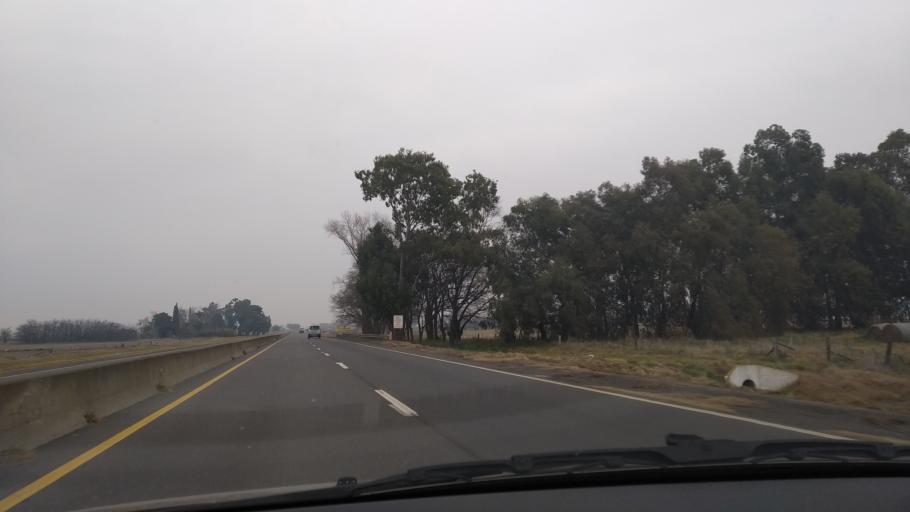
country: AR
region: Buenos Aires
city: Olavarria
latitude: -36.8711
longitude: -60.1347
